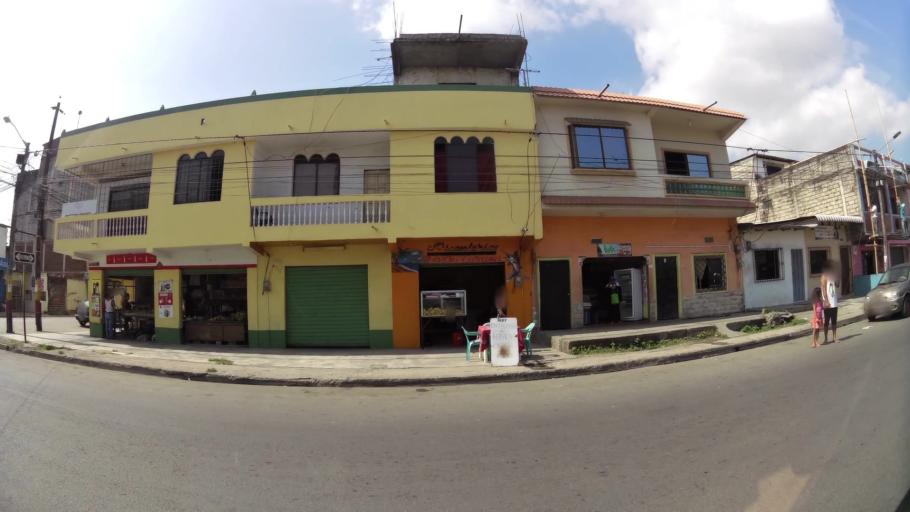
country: EC
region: Guayas
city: Eloy Alfaro
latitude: -2.1544
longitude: -79.8303
